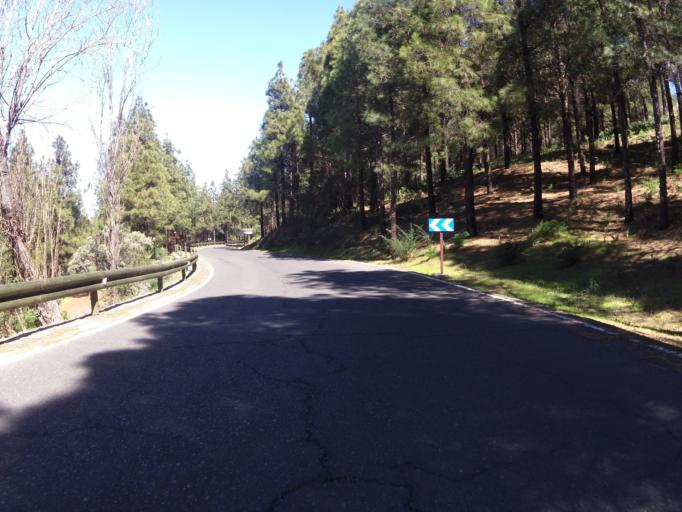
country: ES
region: Canary Islands
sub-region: Provincia de Las Palmas
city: Tejeda
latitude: 27.9861
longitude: -15.5810
